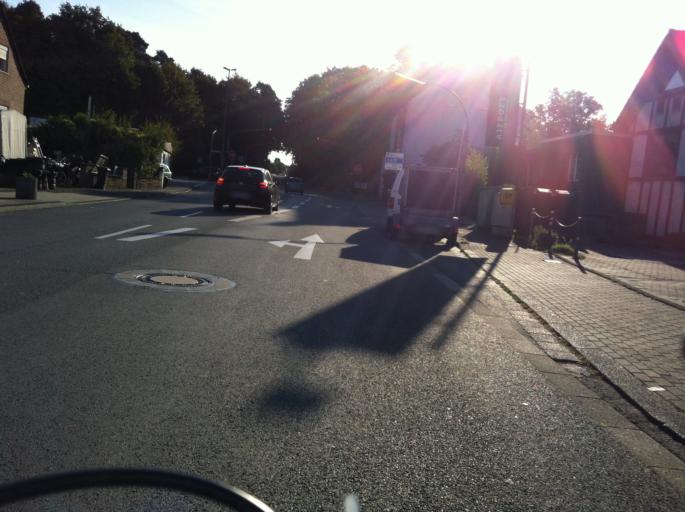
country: DE
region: North Rhine-Westphalia
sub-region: Regierungsbezirk Koln
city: Wahn-Heide
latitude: 50.8802
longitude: 7.1051
